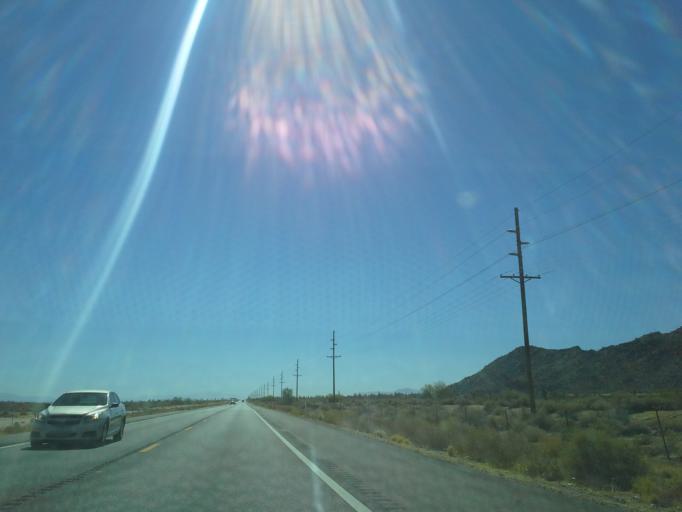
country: US
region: Arizona
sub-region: Pinal County
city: Blackwater
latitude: 33.0398
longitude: -111.6605
